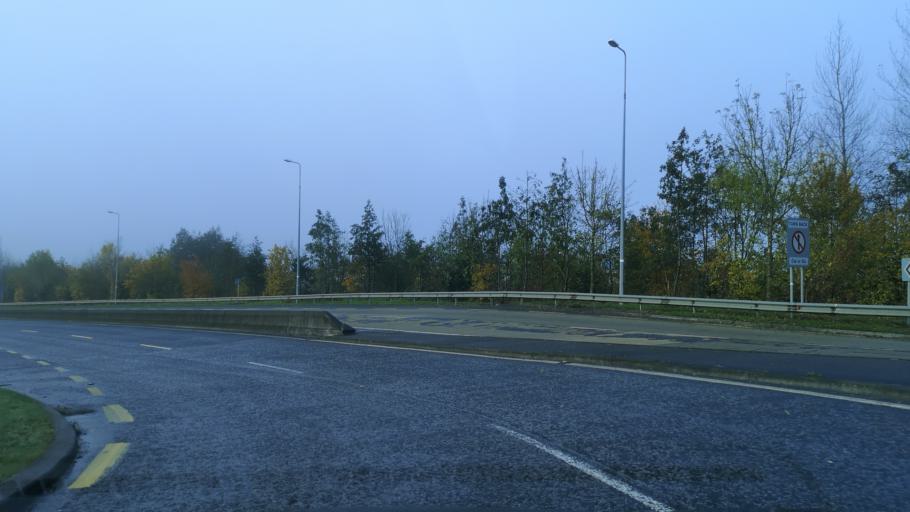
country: IE
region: Leinster
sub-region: An Iarmhi
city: Athlone
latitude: 53.4148
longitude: -7.8904
